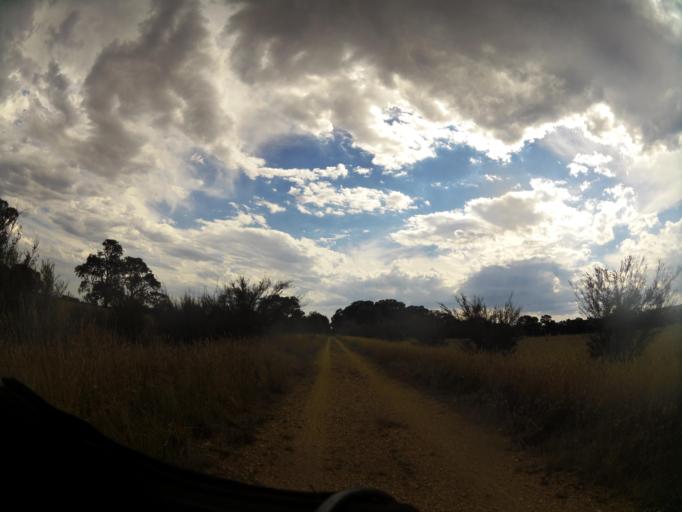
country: AU
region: Victoria
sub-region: Wellington
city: Heyfield
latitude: -38.0328
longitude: 146.6590
